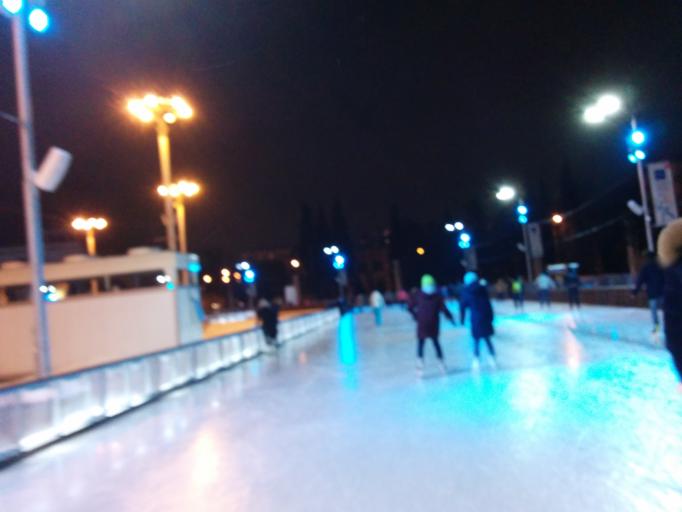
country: RU
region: Moscow
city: Ostankinskiy
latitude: 55.8300
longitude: 37.6304
